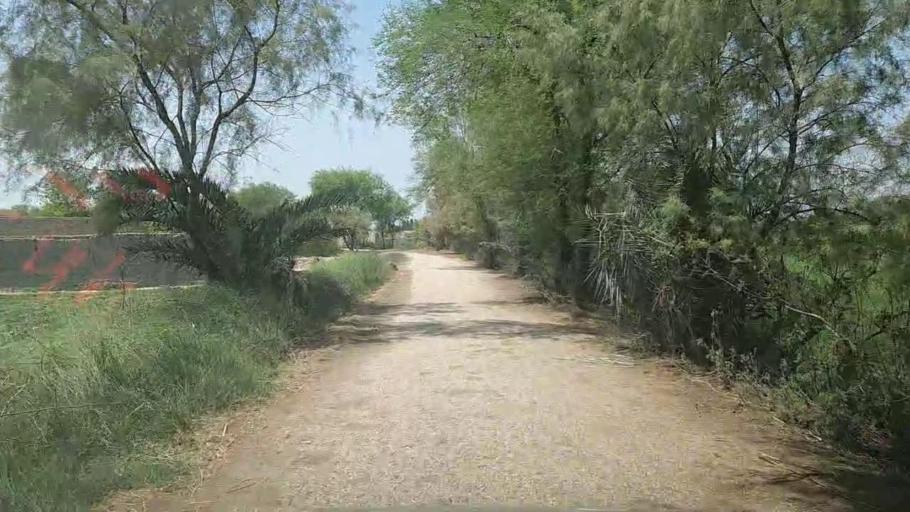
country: PK
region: Sindh
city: Ubauro
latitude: 28.1784
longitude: 69.7091
